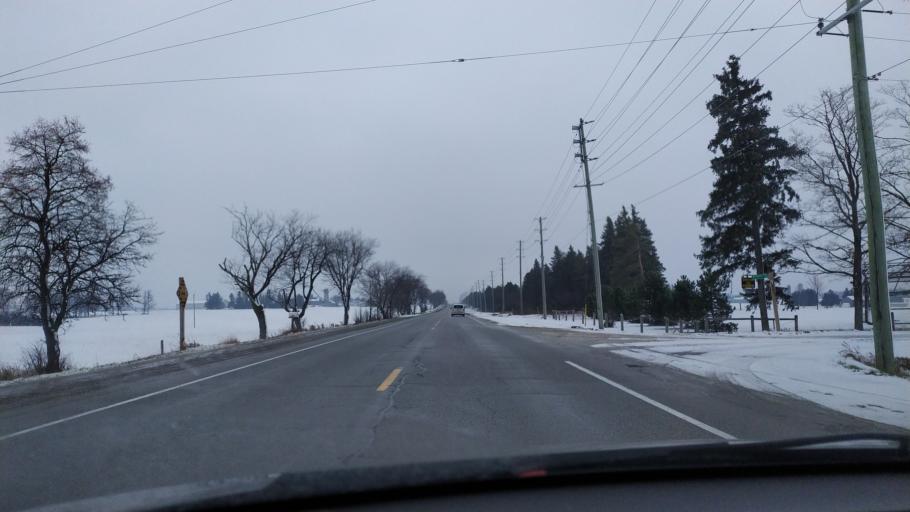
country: CA
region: Ontario
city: Waterloo
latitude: 43.6160
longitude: -80.6753
